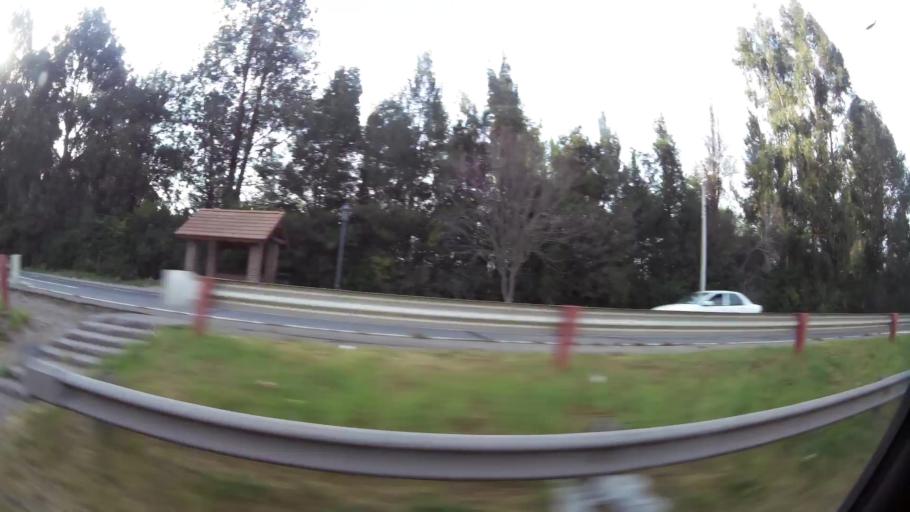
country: CL
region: Santiago Metropolitan
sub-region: Provincia de Talagante
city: Penaflor
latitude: -33.5813
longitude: -70.8291
